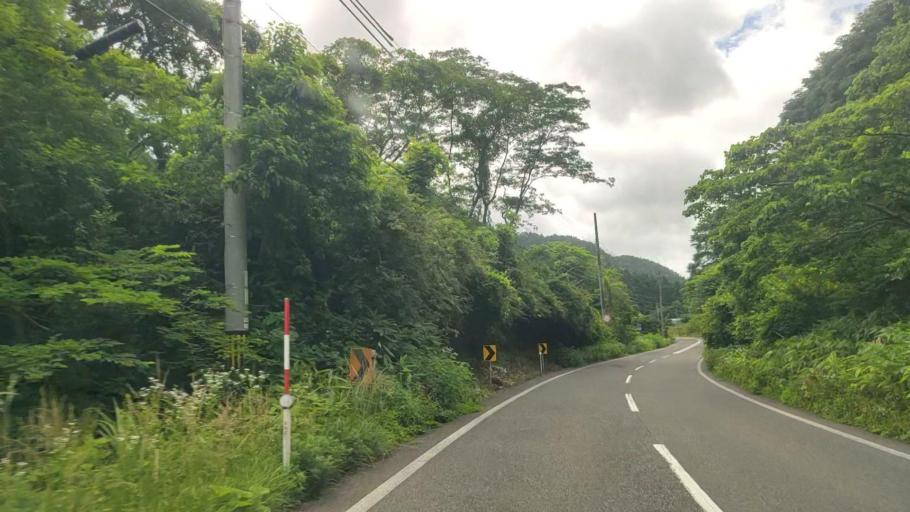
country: JP
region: Tottori
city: Yonago
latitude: 35.2792
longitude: 133.4302
